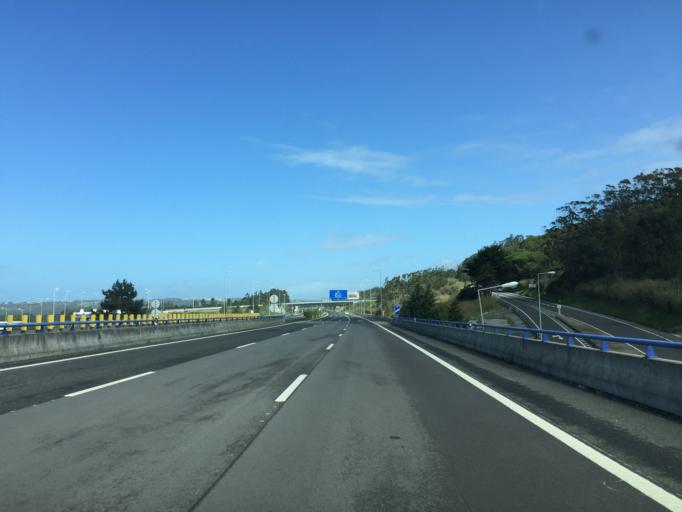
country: PT
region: Leiria
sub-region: Caldas da Rainha
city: Caldas da Rainha
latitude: 39.4975
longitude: -9.0915
